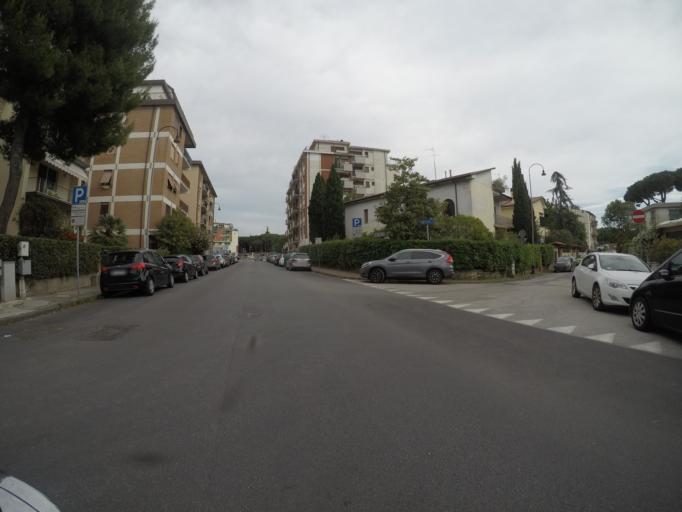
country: IT
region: Tuscany
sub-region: Province of Pisa
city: Pisa
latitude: 43.7207
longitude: 10.4108
